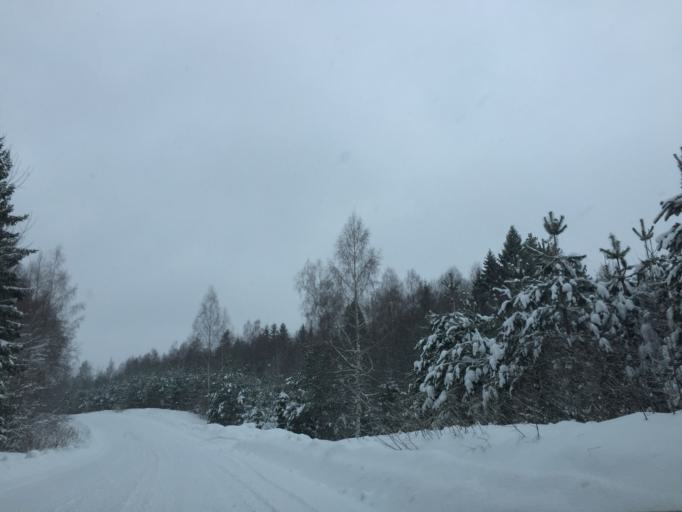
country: LV
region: Amatas Novads
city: Drabesi
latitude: 57.1650
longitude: 25.2951
